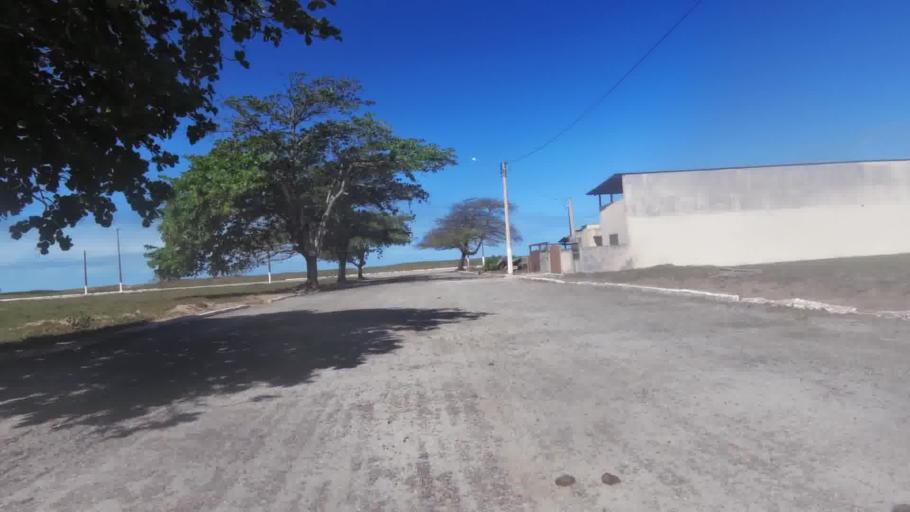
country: BR
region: Espirito Santo
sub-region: Marataizes
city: Marataizes
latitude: -21.1936
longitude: -40.9313
